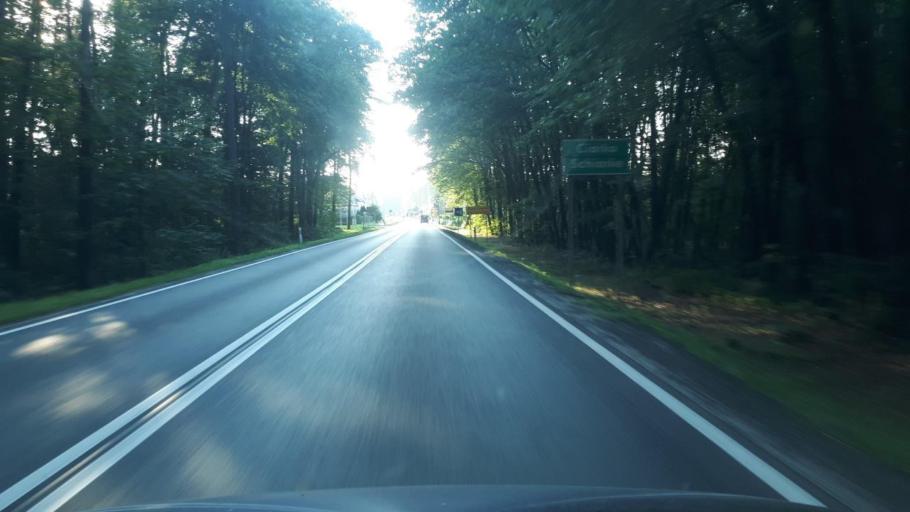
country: PL
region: Opole Voivodeship
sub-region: Powiat kluczborski
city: Kluczbork
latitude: 50.9453
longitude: 18.3204
